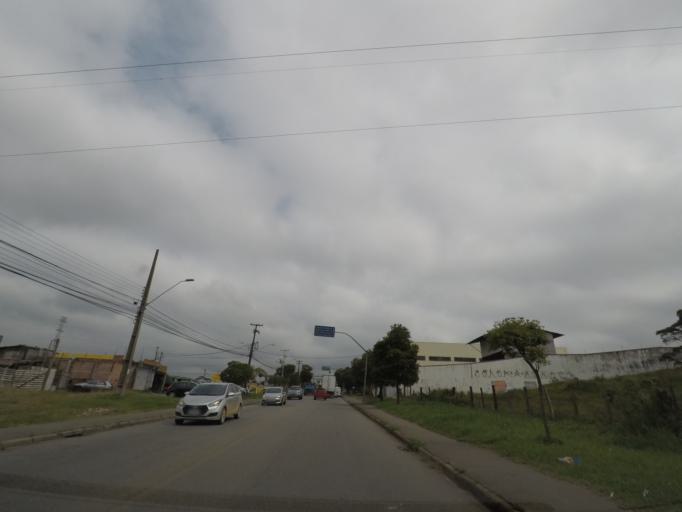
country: BR
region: Parana
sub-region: Curitiba
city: Curitiba
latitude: -25.4951
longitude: -49.3413
